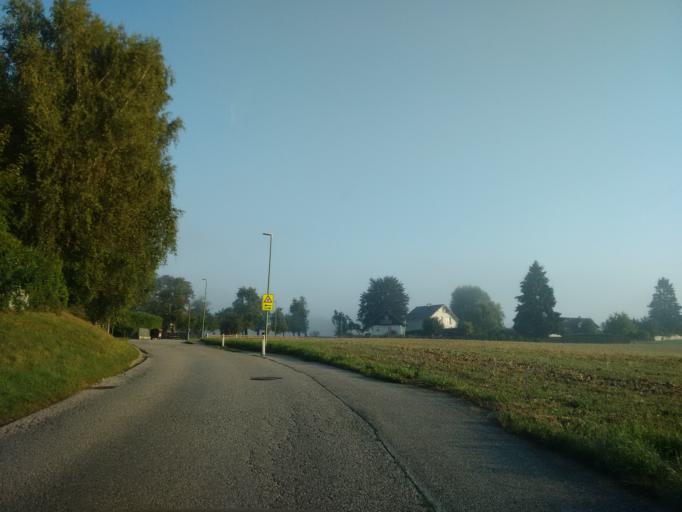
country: AT
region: Upper Austria
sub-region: Wels-Land
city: Buchkirchen
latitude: 48.1905
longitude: 14.0009
